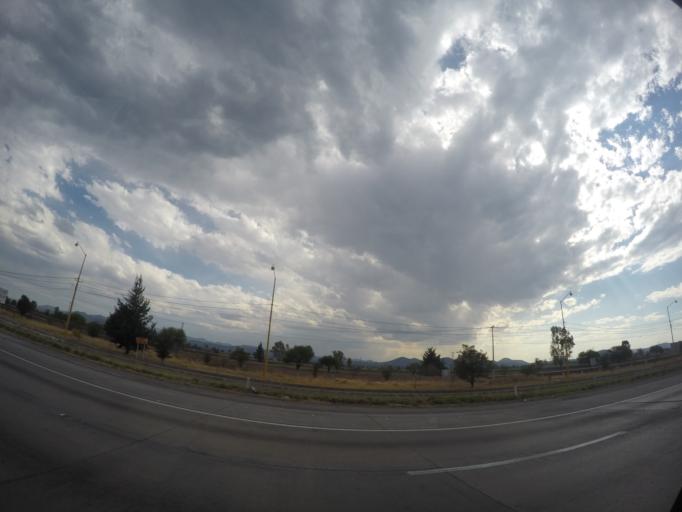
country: MX
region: Queretaro
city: La Estancia
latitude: 20.4179
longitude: -100.0462
